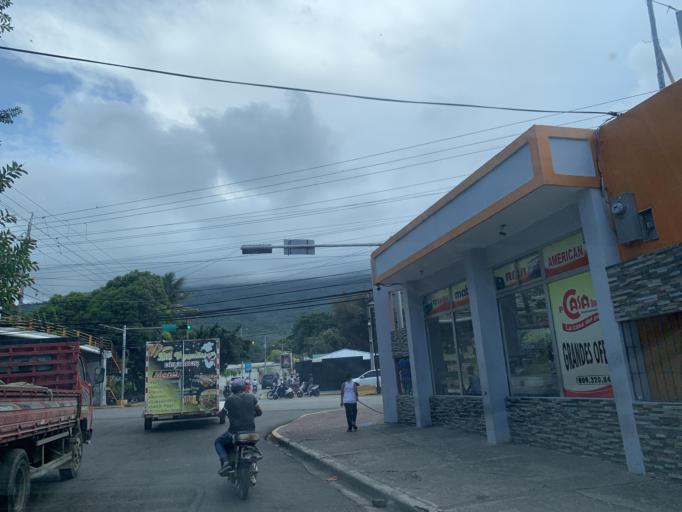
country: DO
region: Puerto Plata
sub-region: Puerto Plata
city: Puerto Plata
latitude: 19.7884
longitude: -70.6969
